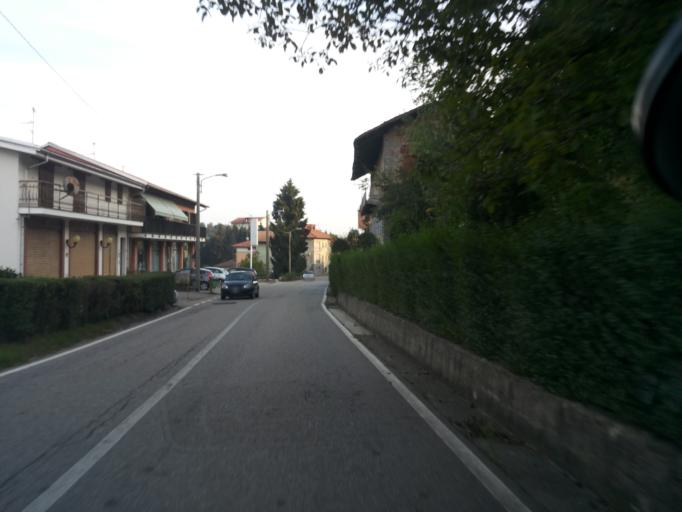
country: IT
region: Piedmont
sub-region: Provincia di Biella
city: Valle Mosso
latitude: 45.6437
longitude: 8.1526
